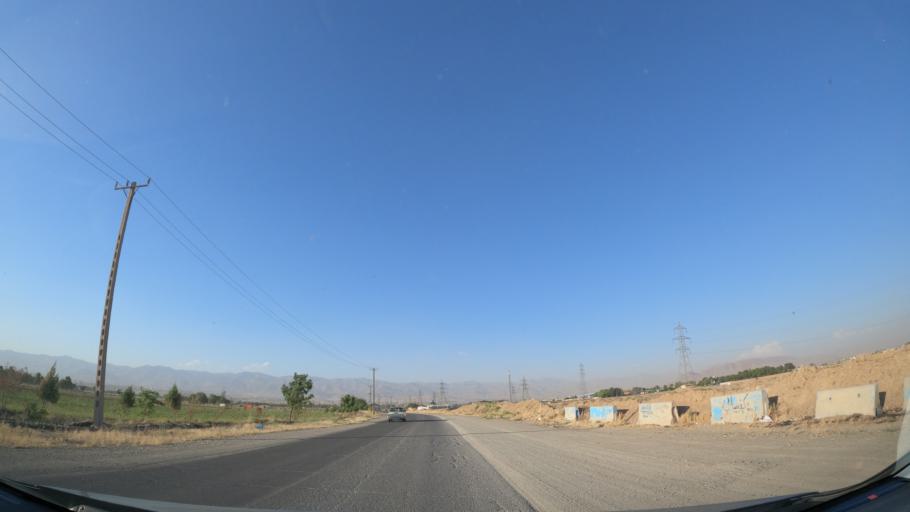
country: IR
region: Alborz
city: Hashtgerd
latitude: 35.9203
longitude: 50.7389
